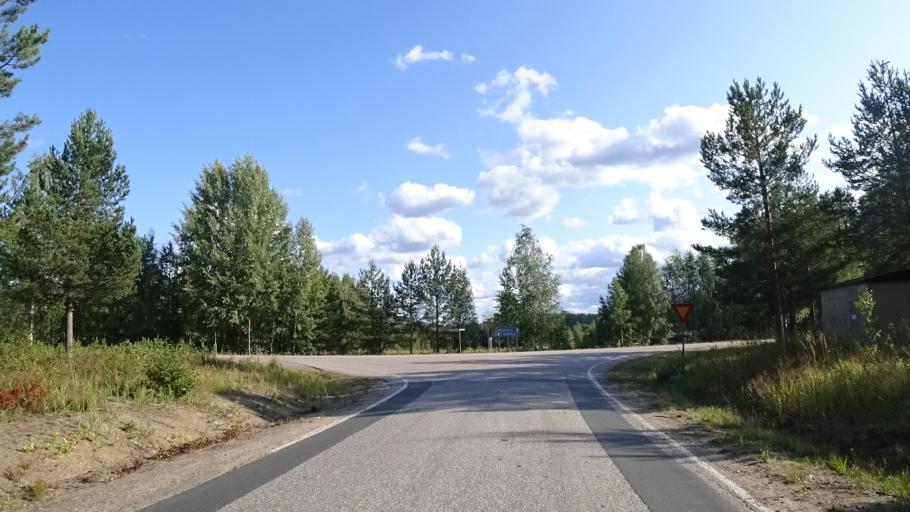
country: FI
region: North Karelia
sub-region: Keski-Karjala
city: Kesaelahti
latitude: 61.8950
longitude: 29.8501
